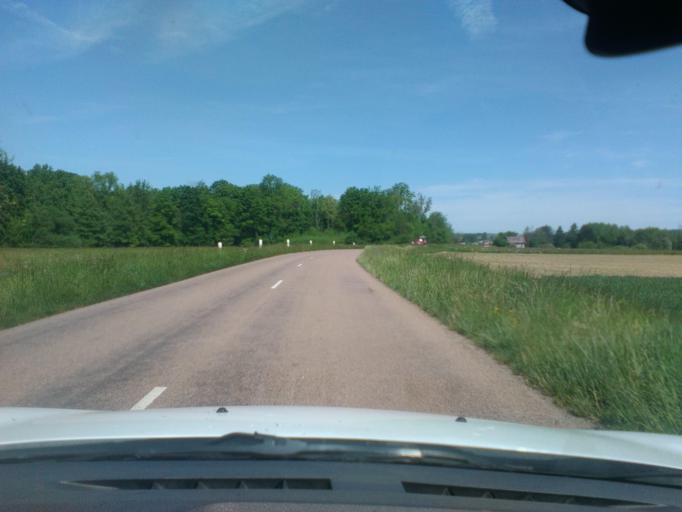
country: FR
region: Lorraine
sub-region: Departement de Meurthe-et-Moselle
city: Gerbeviller
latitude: 48.4259
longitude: 6.5802
